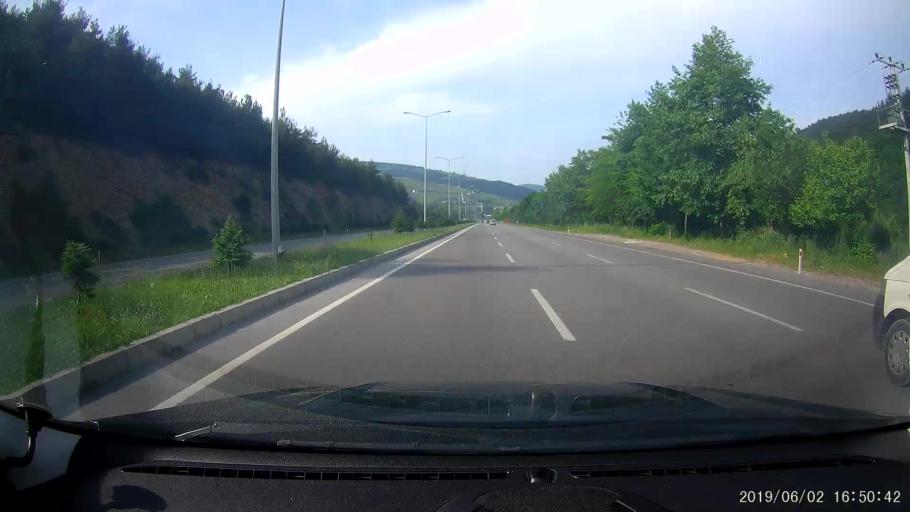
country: TR
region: Samsun
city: Taflan
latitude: 41.2603
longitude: 36.1749
